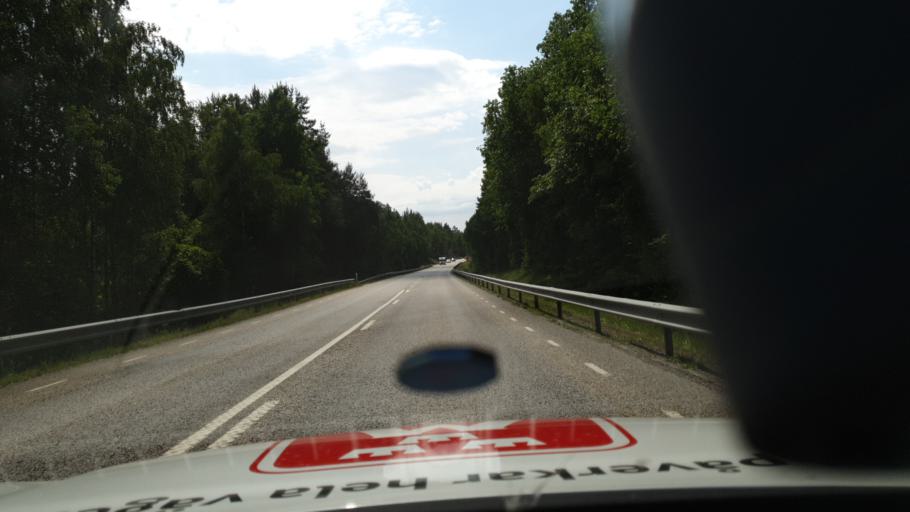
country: SE
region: Joenkoeping
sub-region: Habo Kommun
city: Habo
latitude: 57.9189
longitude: 14.0979
